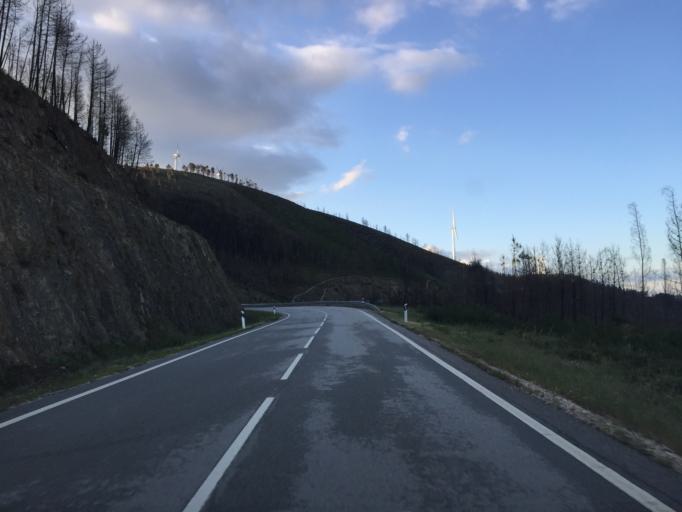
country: PT
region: Coimbra
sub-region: Gois
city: Gois
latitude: 40.0934
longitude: -8.0551
